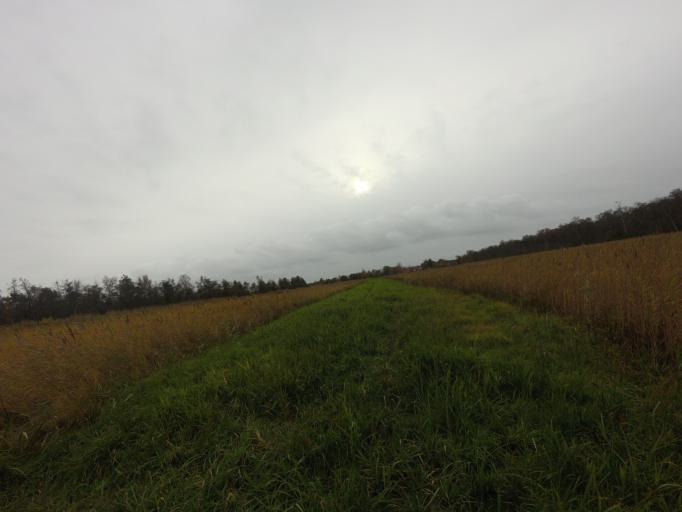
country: NL
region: Overijssel
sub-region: Gemeente Steenwijkerland
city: Oldemarkt
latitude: 52.7801
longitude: 5.9621
